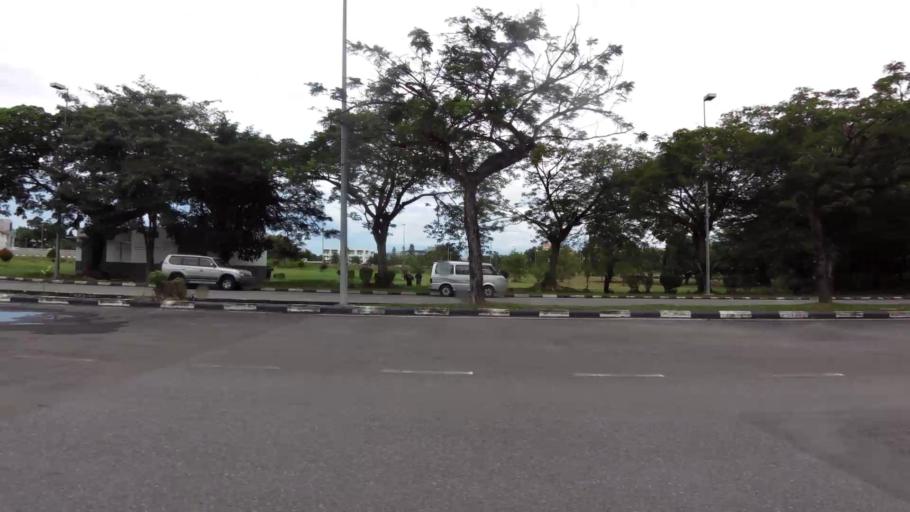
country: BN
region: Brunei and Muara
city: Bandar Seri Begawan
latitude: 4.8993
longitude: 114.9209
